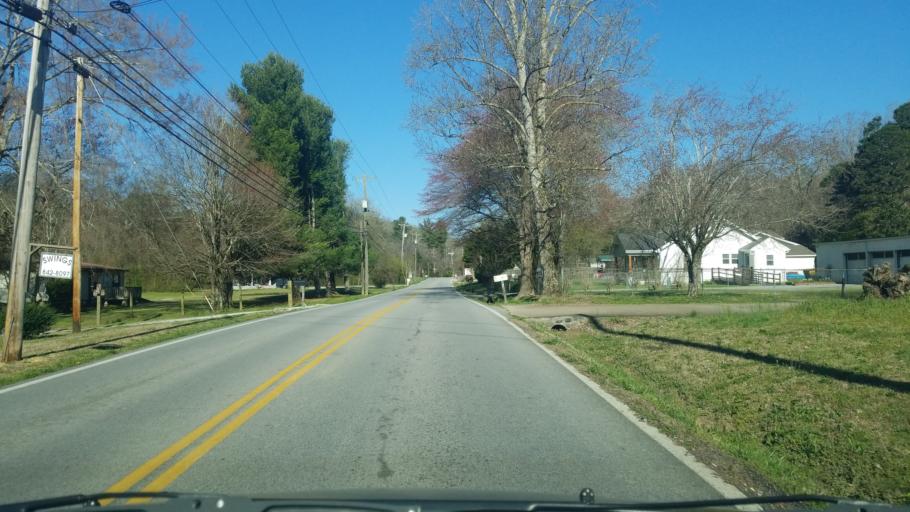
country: US
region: Tennessee
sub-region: Hamilton County
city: Middle Valley
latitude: 35.2069
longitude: -85.1684
